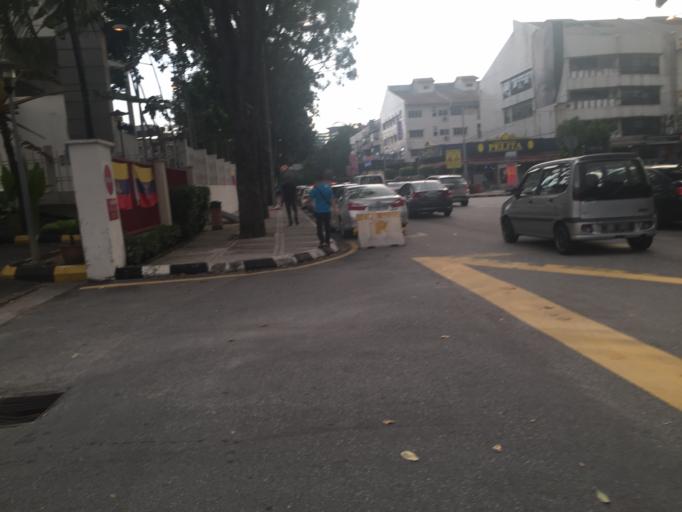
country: MY
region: Kuala Lumpur
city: Kuala Lumpur
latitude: 3.1623
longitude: 101.6506
